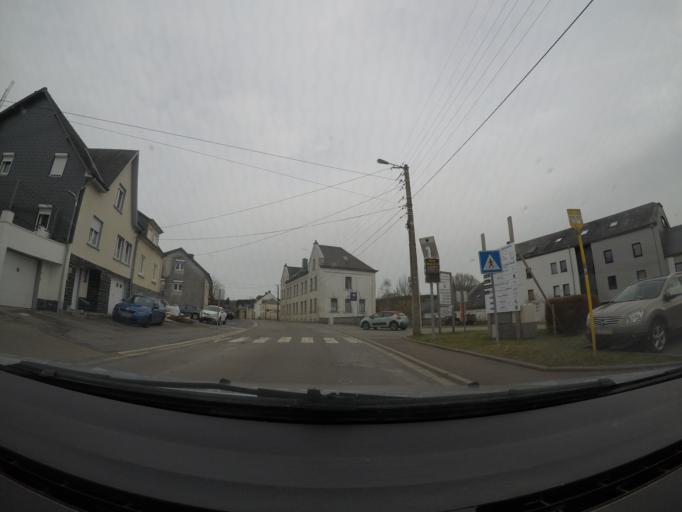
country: BE
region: Wallonia
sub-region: Province du Luxembourg
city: Martelange
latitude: 49.8321
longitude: 5.7304
